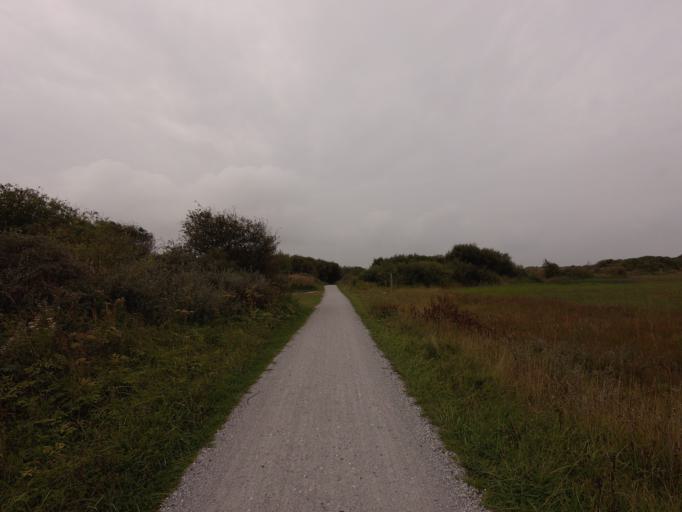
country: NL
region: Friesland
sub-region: Gemeente Schiermonnikoog
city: Schiermonnikoog
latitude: 53.4947
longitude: 6.1936
